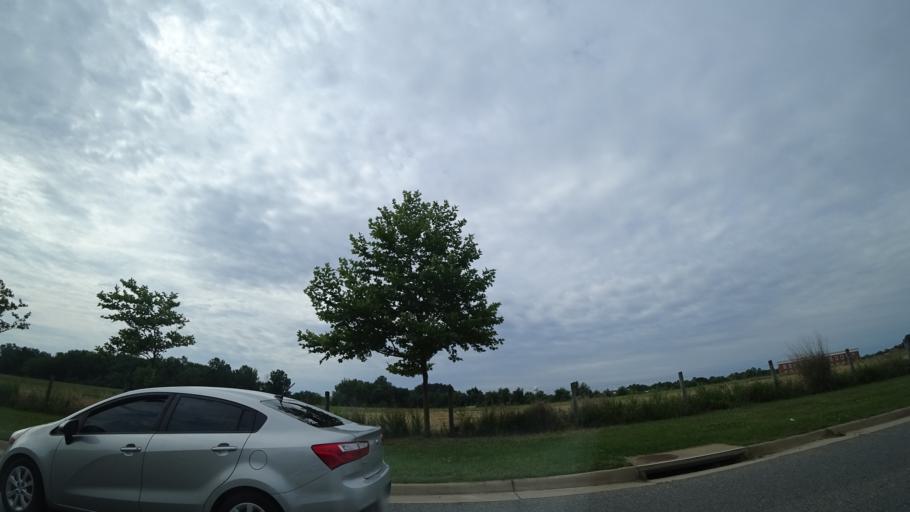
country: US
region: Virginia
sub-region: Spotsylvania County
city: Spotsylvania
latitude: 38.2064
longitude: -77.5903
